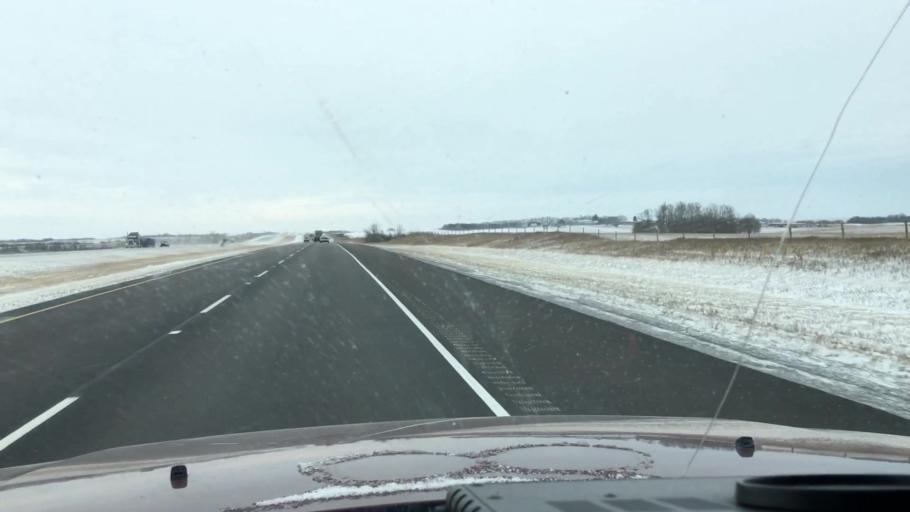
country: CA
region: Saskatchewan
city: Saskatoon
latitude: 51.6966
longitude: -106.4600
